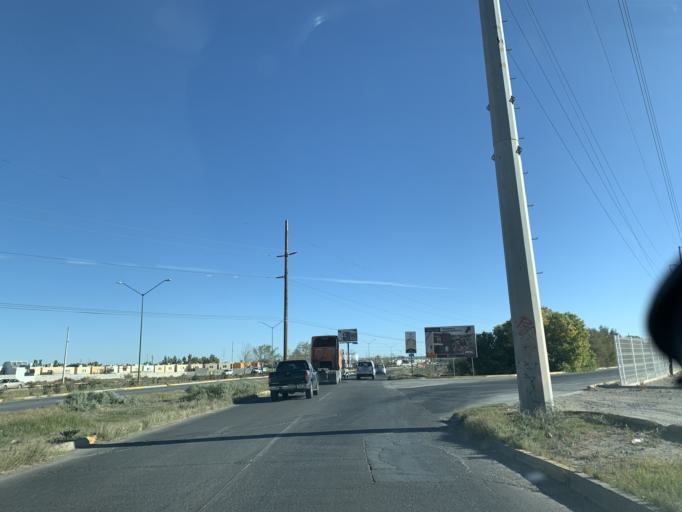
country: US
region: Texas
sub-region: El Paso County
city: Socorro
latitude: 31.7081
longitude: -106.3802
